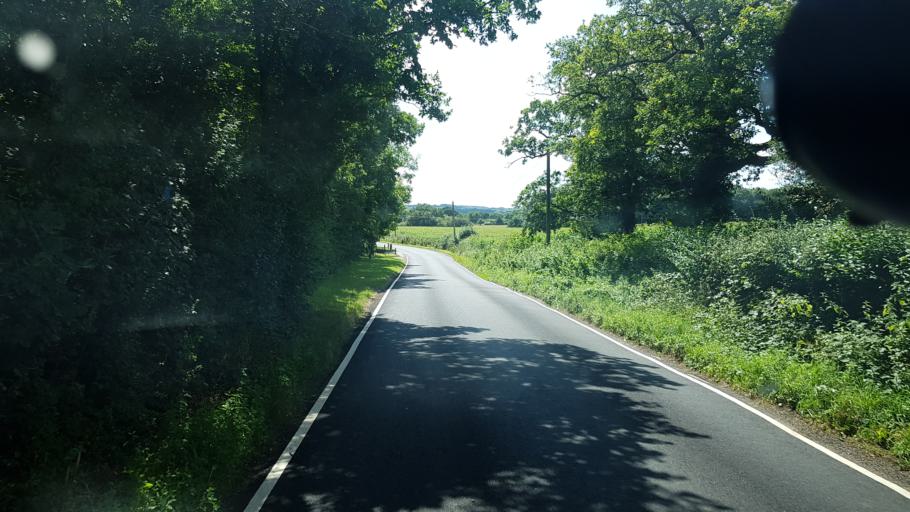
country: GB
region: England
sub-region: Kent
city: Edenbridge
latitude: 51.2083
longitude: 0.1272
